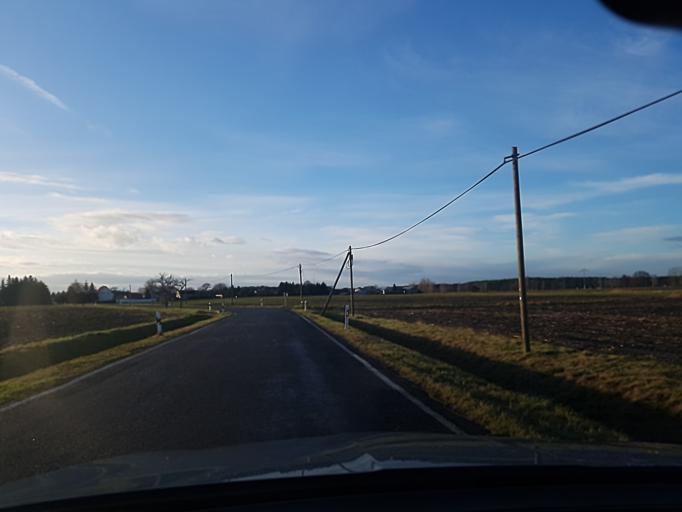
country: DE
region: Brandenburg
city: Schilda
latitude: 51.5882
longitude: 13.3924
